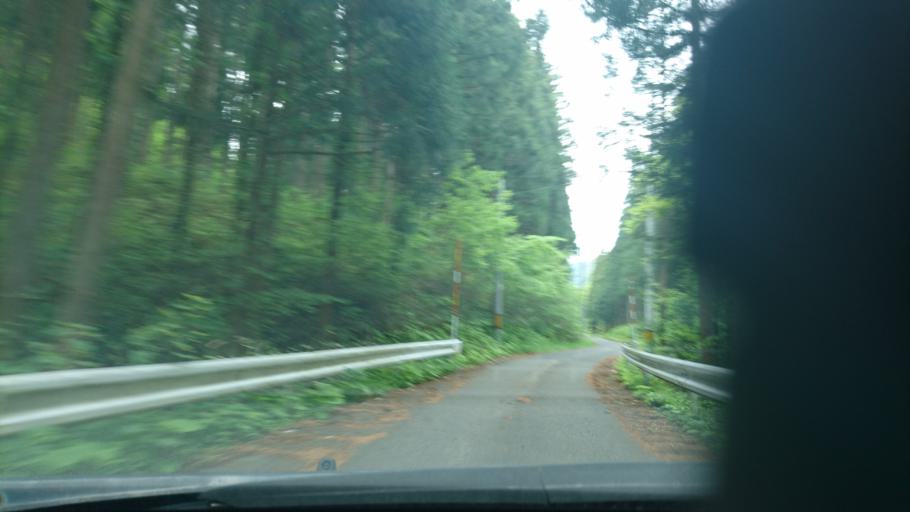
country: JP
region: Iwate
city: Ichinoseki
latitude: 38.9043
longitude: 140.9132
